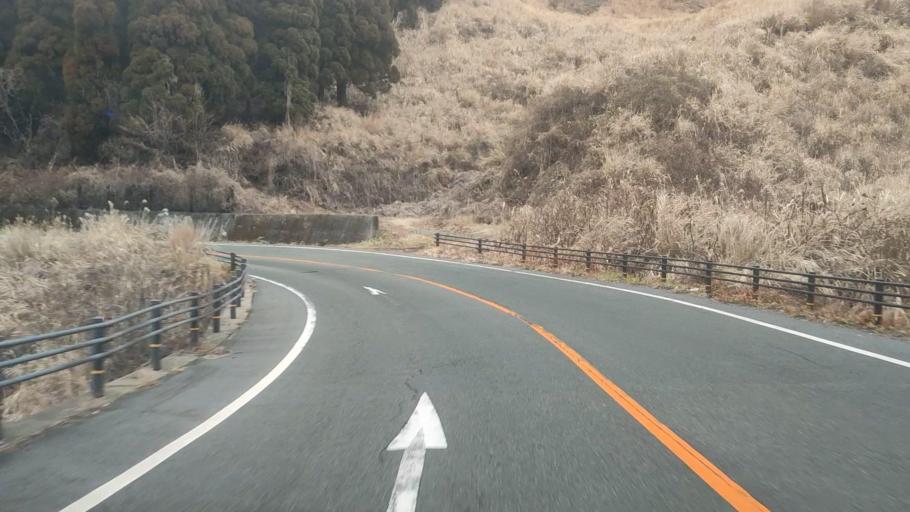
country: JP
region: Kumamoto
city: Aso
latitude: 32.9074
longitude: 131.1447
